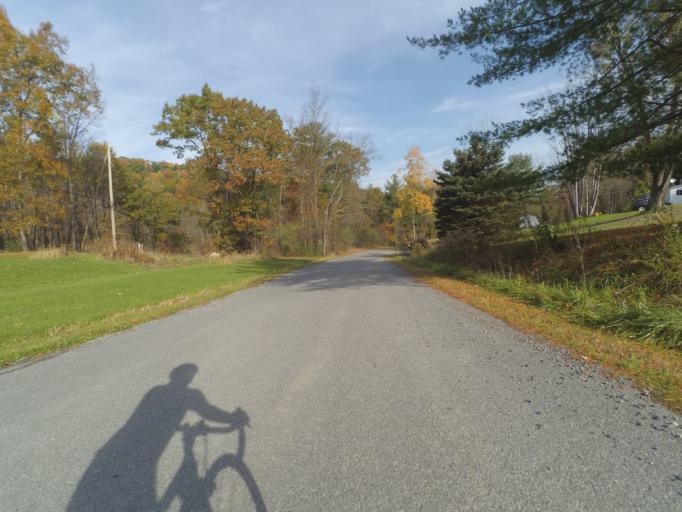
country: US
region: Pennsylvania
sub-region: Centre County
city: Park Forest Village
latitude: 40.9188
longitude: -77.9071
